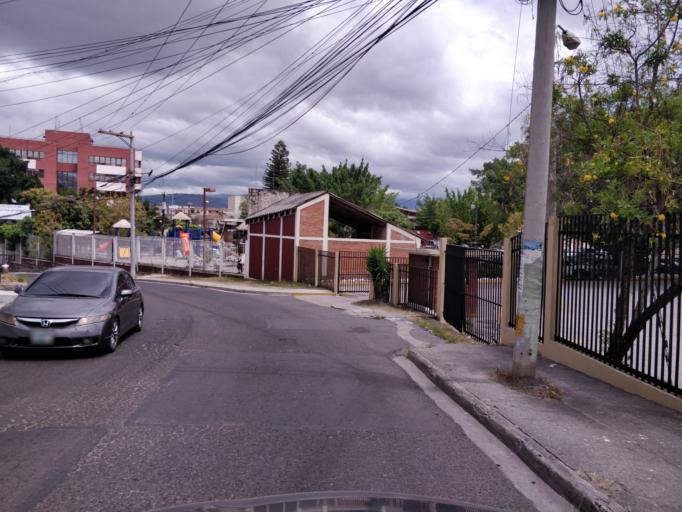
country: HN
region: Francisco Morazan
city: Yaguacire
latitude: 14.0457
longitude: -87.2206
